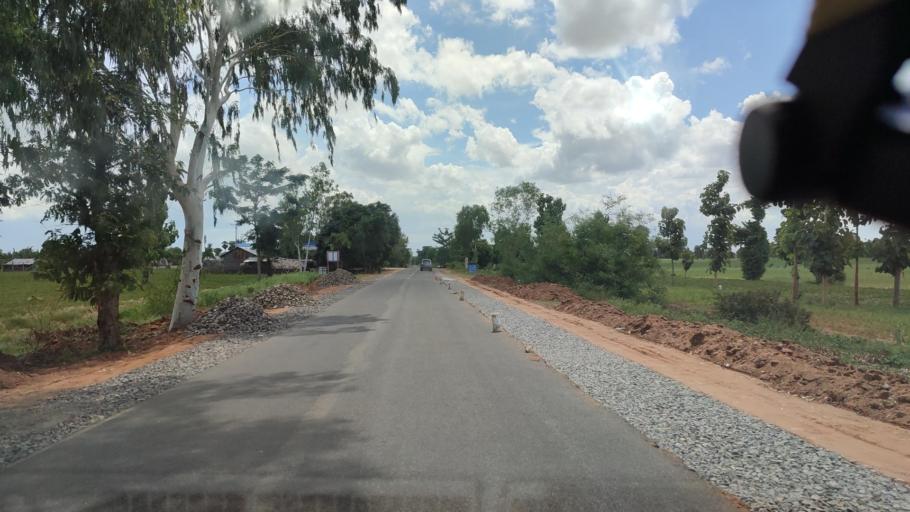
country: MM
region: Magway
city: Magway
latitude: 20.1912
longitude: 95.0586
